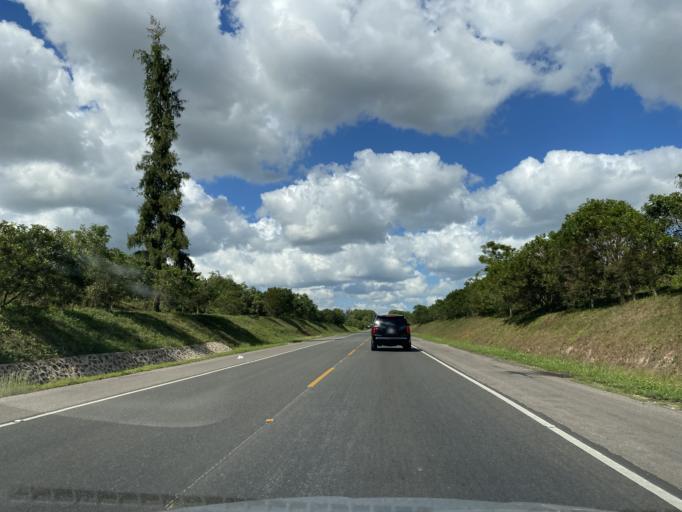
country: DO
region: Monte Plata
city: Monte Plata
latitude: 18.7433
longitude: -69.7645
